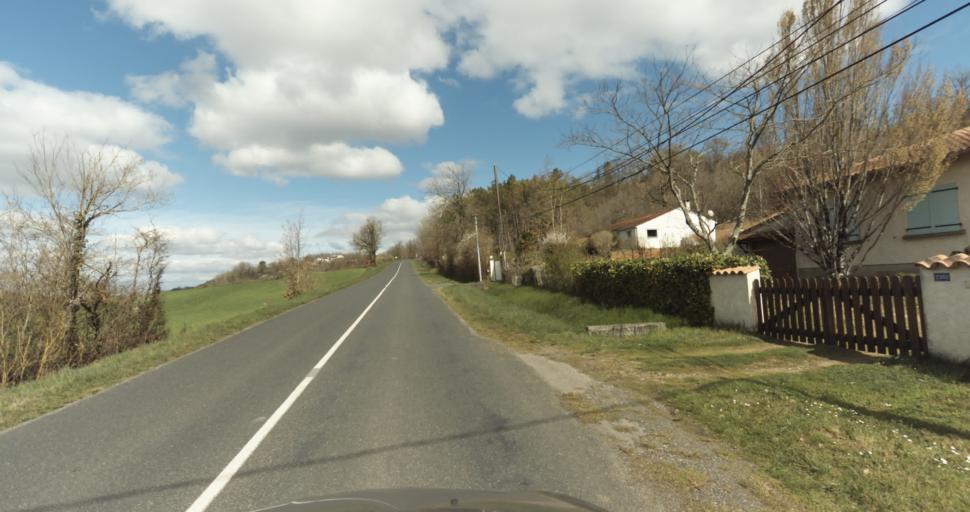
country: FR
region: Midi-Pyrenees
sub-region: Departement du Tarn
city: Puygouzon
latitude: 43.8782
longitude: 2.1555
